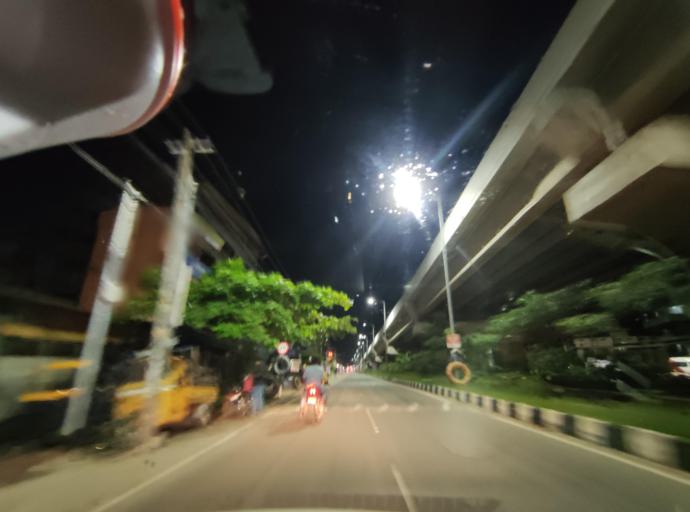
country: IN
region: Kerala
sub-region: Thiruvananthapuram
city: Thiruvananthapuram
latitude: 8.4861
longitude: 76.9285
